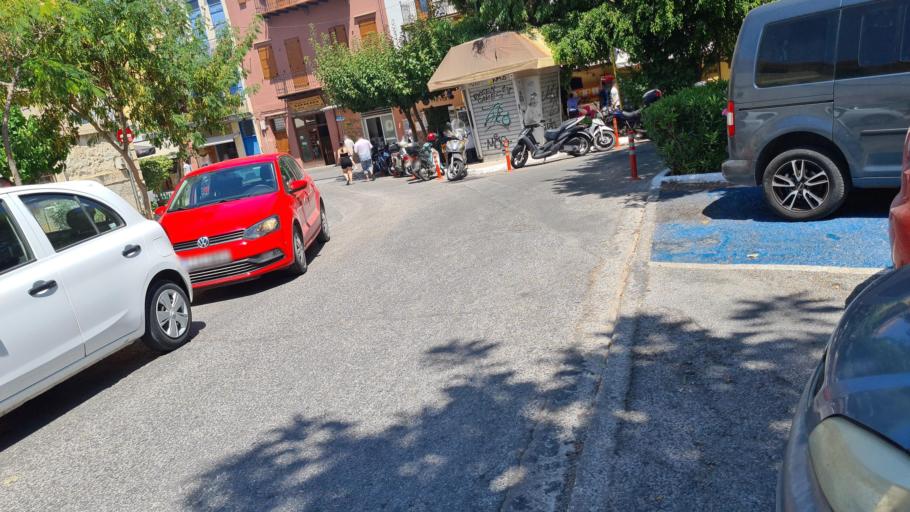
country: GR
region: Crete
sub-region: Nomos Chanias
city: Chania
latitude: 35.5148
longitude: 24.0209
